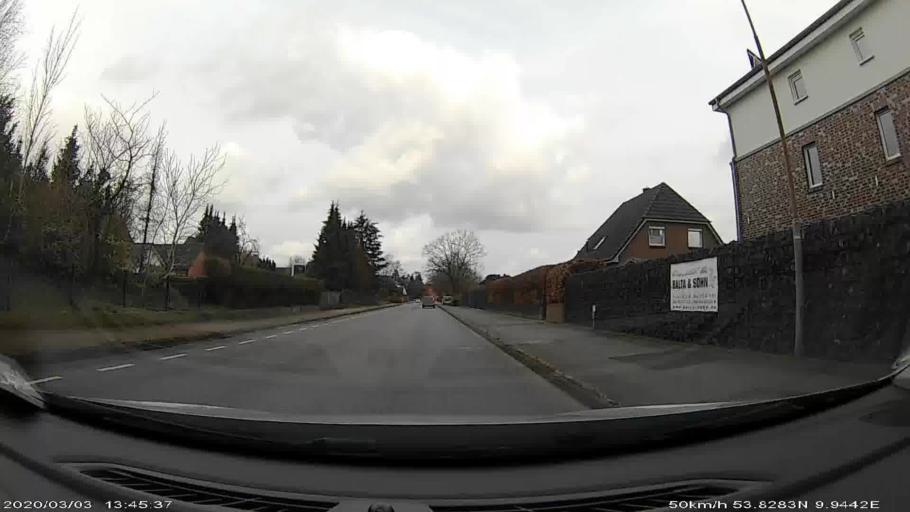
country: DE
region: Schleswig-Holstein
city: Kaltenkirchen
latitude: 53.8290
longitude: 9.9451
